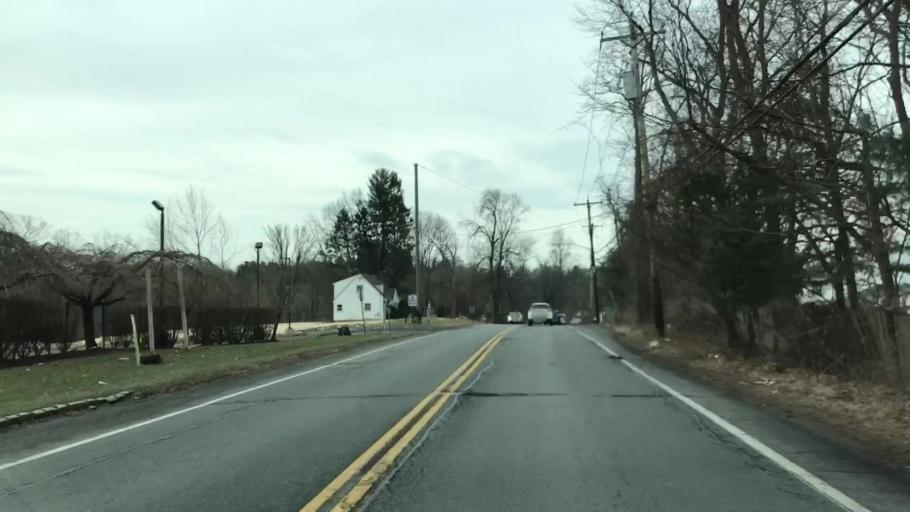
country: US
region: New York
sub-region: Rockland County
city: New Square
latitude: 41.1394
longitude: -74.0356
